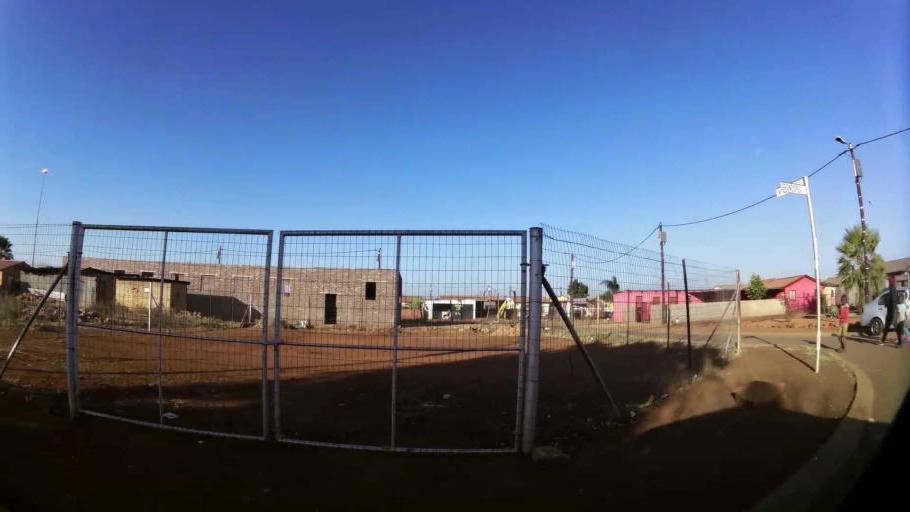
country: ZA
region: Gauteng
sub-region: City of Tshwane Metropolitan Municipality
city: Mabopane
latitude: -25.5975
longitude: 28.1030
